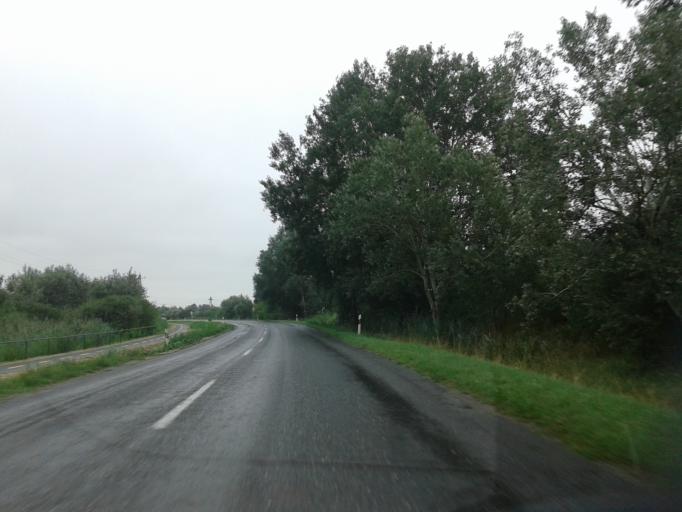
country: HU
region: Bacs-Kiskun
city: Akaszto
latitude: 46.7040
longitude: 19.1885
